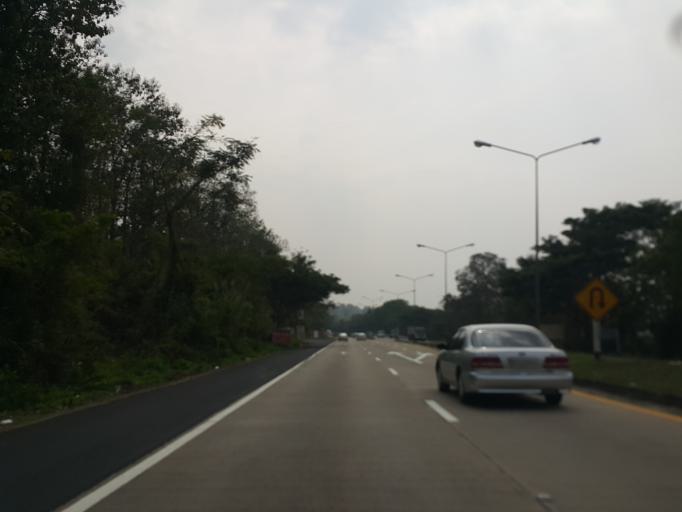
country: TH
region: Lampang
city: Hang Chat
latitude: 18.3293
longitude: 99.2633
